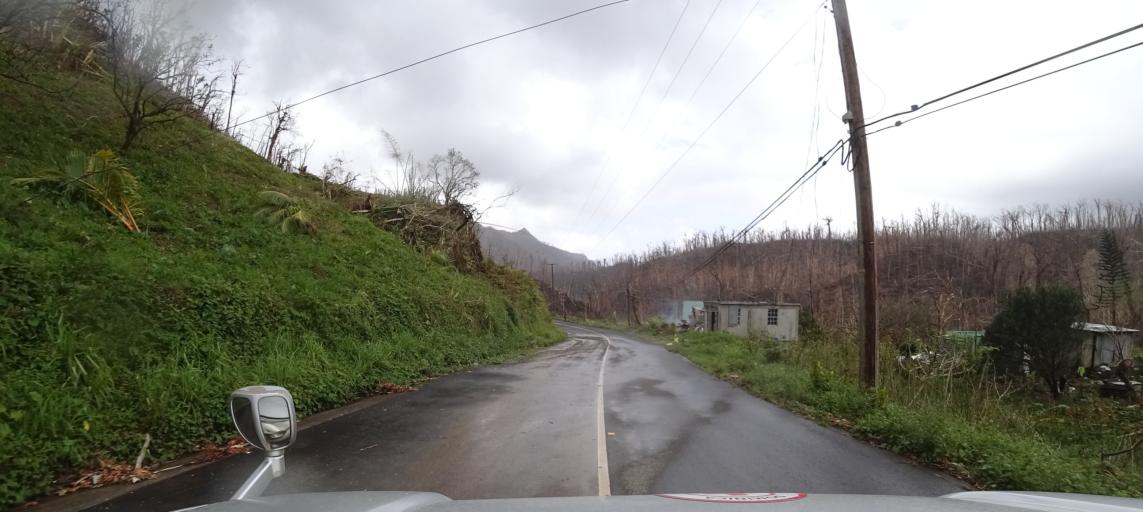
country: DM
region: Saint Paul
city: Pont Casse
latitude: 15.4289
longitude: -61.3360
